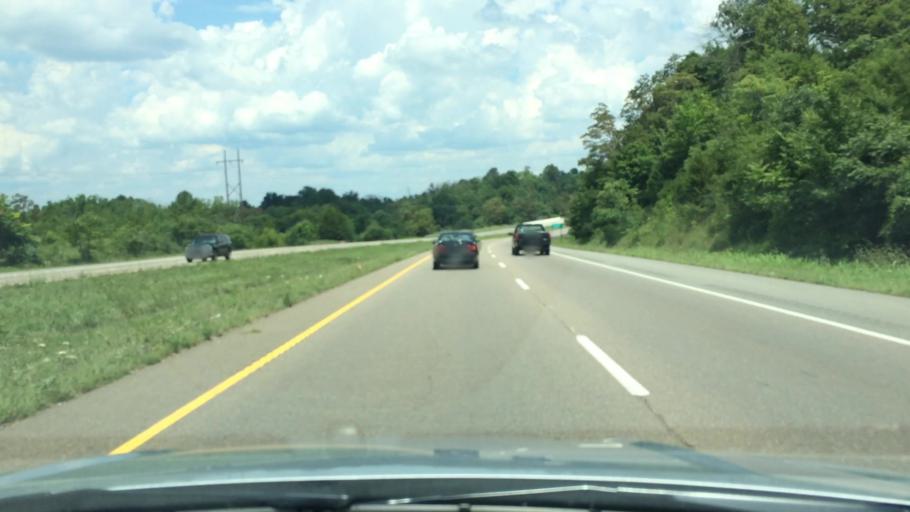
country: US
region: Tennessee
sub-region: Hamblen County
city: Morristown
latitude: 36.1866
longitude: -83.3106
